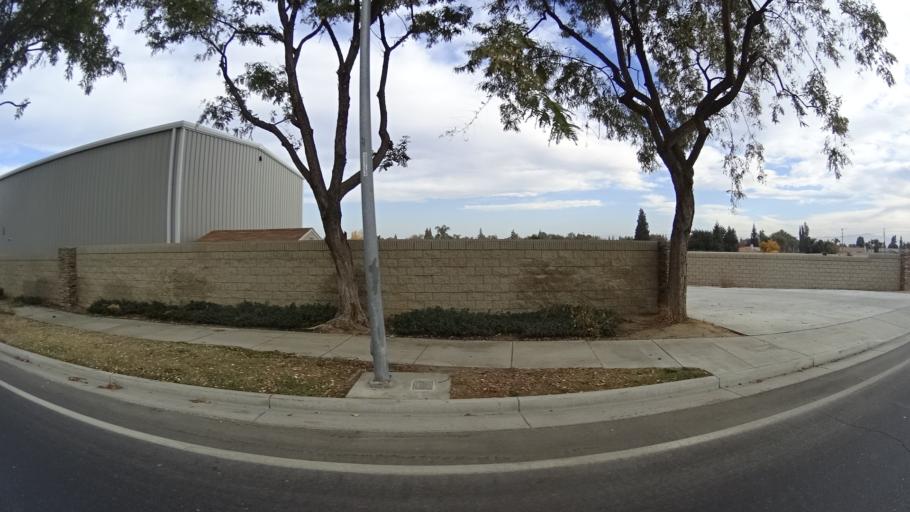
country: US
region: California
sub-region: Kern County
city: Greenacres
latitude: 35.4132
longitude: -119.1126
